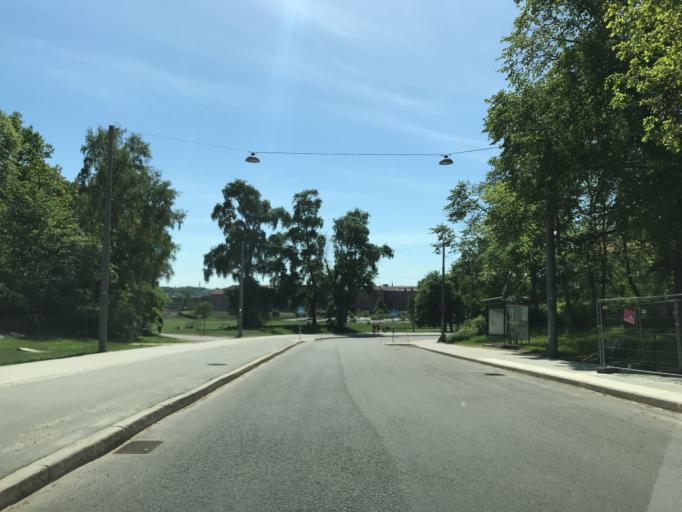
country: SE
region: Stockholm
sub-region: Stockholms Kommun
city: OEstermalm
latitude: 59.3456
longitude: 18.1016
